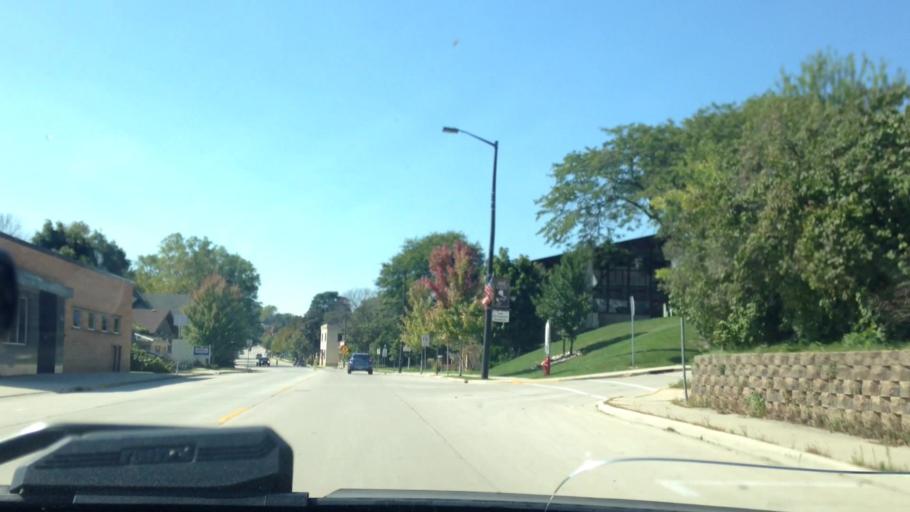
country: US
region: Wisconsin
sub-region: Ozaukee County
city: Port Washington
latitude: 43.3876
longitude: -87.8738
